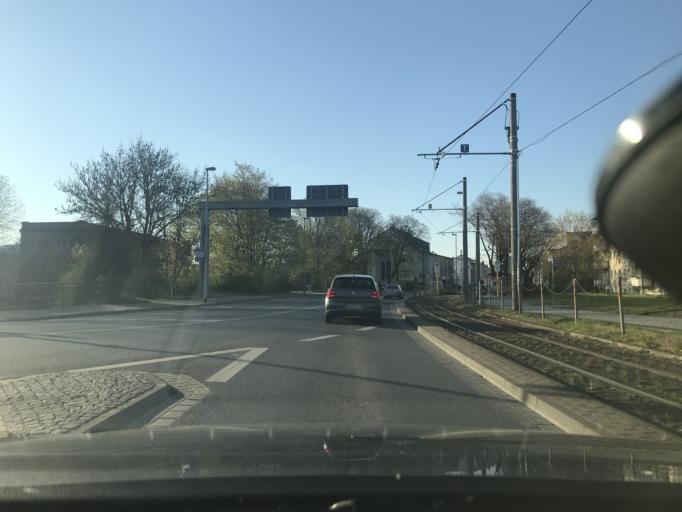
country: DE
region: Thuringia
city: Nordhausen
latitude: 51.4982
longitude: 10.7892
